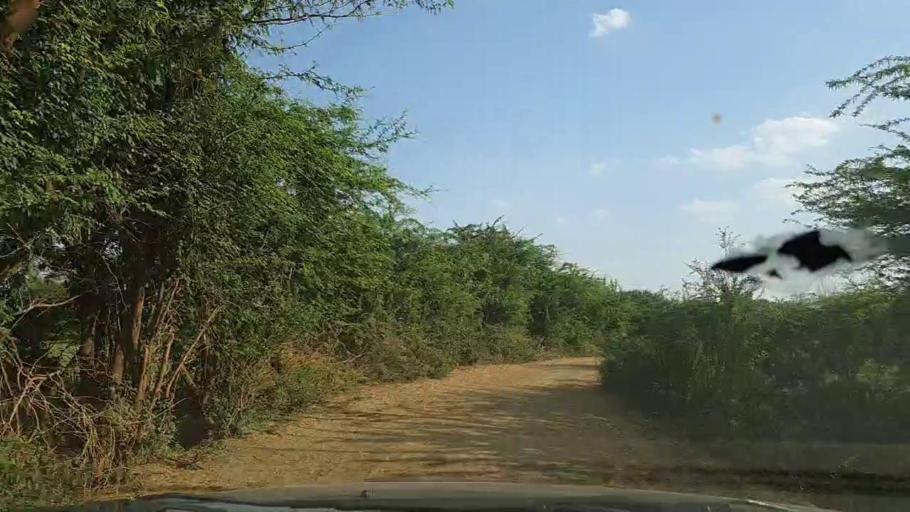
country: PK
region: Sindh
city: Daro Mehar
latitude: 24.8308
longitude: 68.0987
